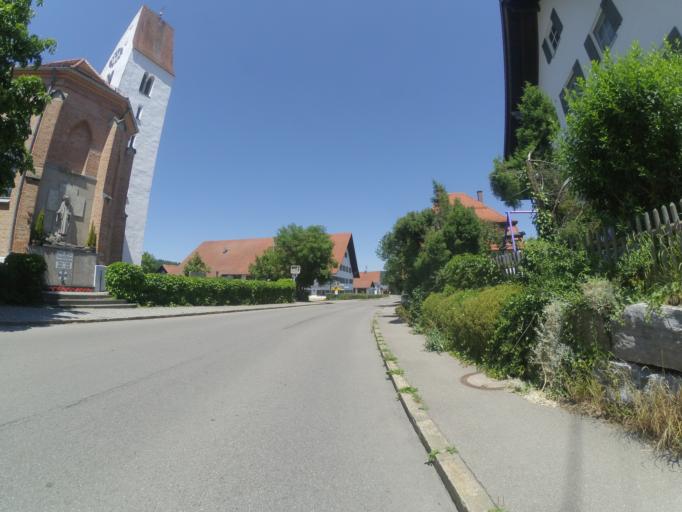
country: DE
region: Bavaria
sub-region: Swabia
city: Untrasried
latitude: 47.8539
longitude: 10.3548
